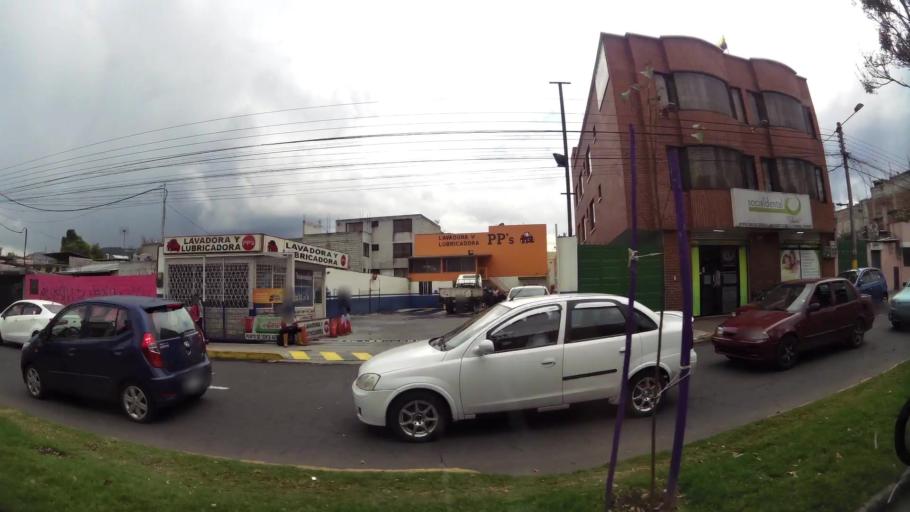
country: EC
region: Pichincha
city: Quito
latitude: -0.2734
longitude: -78.5430
